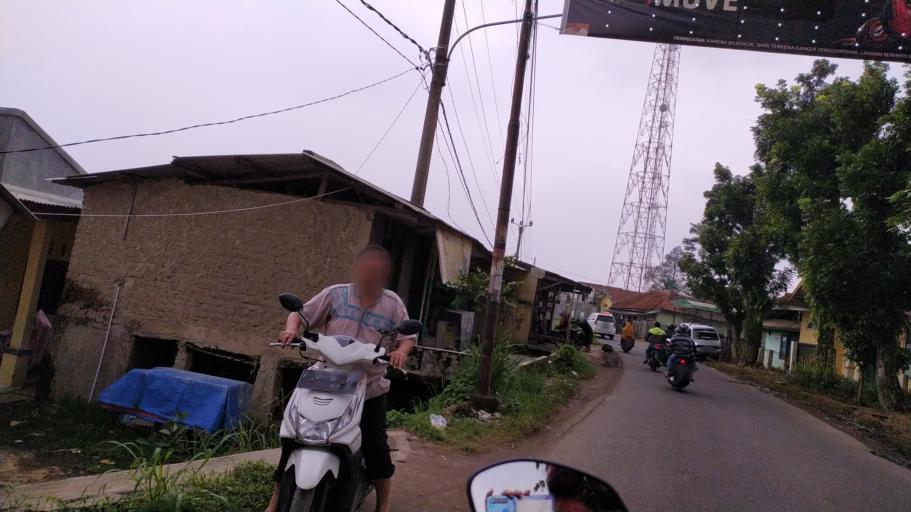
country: ID
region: West Java
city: Ciampea
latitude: -6.6051
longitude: 106.7011
